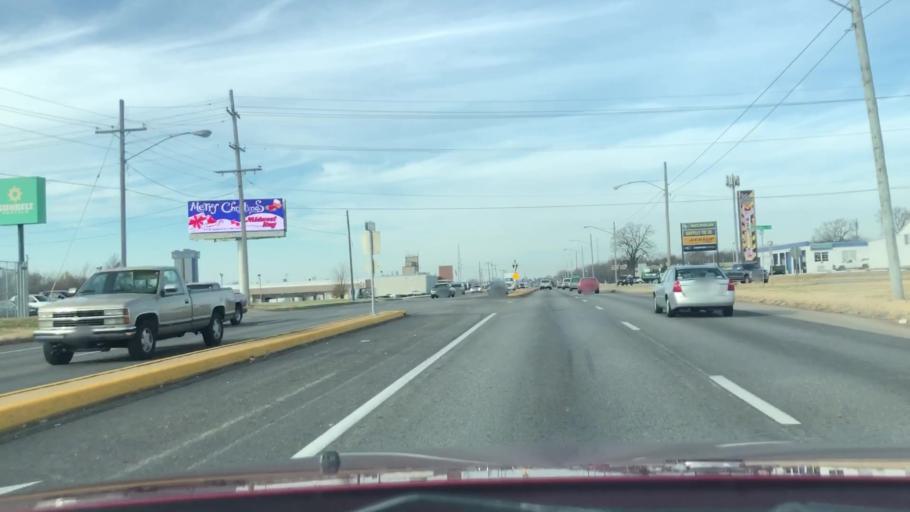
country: US
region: Missouri
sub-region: Greene County
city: Springfield
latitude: 37.2148
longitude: -93.2658
